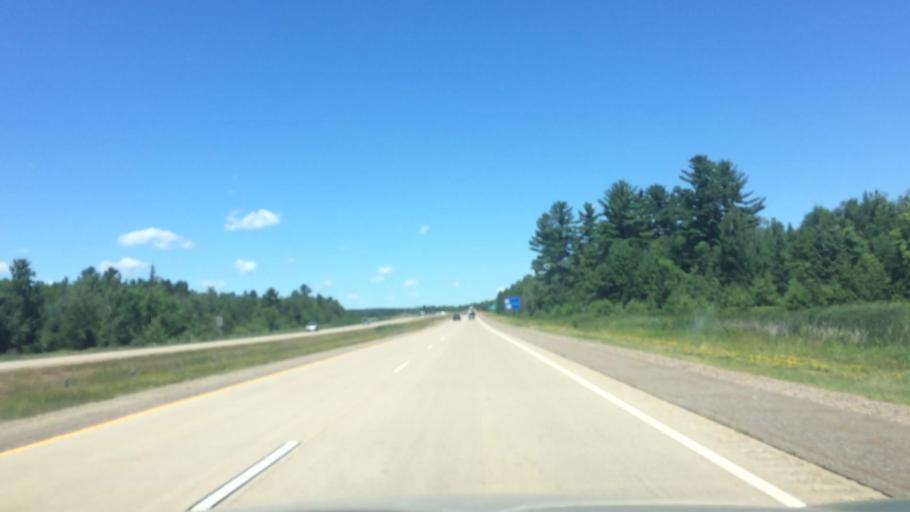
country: US
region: Wisconsin
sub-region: Lincoln County
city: Tomahawk
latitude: 45.4078
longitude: -89.6716
